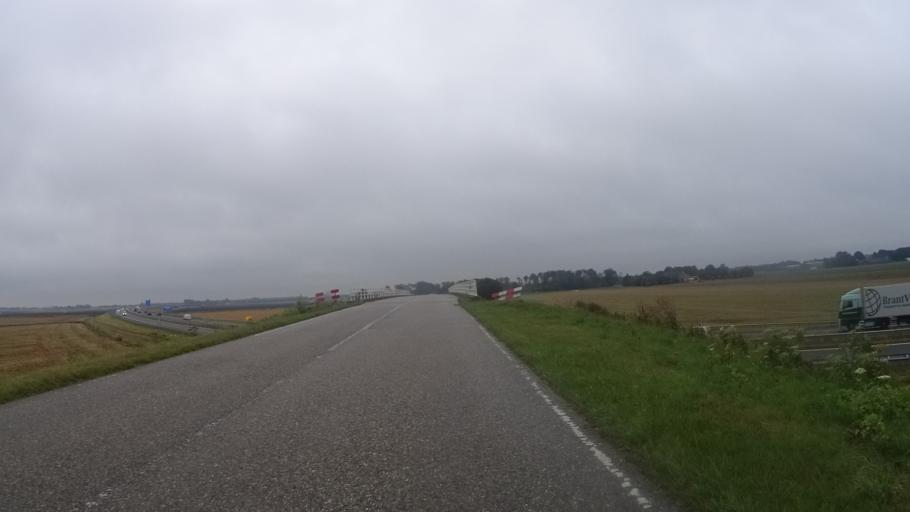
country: NL
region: Groningen
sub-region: Gemeente  Oldambt
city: Winschoten
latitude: 53.1867
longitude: 6.9438
